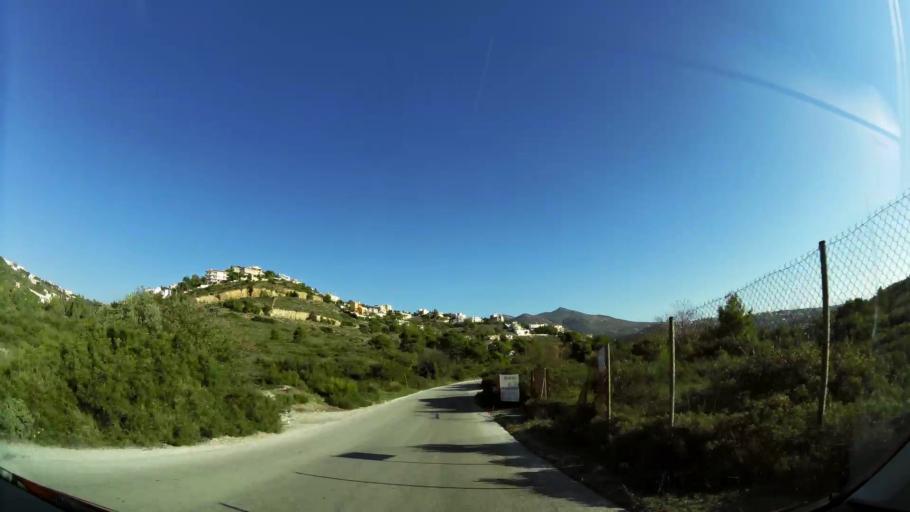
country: GR
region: Attica
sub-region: Nomarchia Anatolikis Attikis
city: Dhrafi
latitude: 38.0179
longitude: 23.9029
